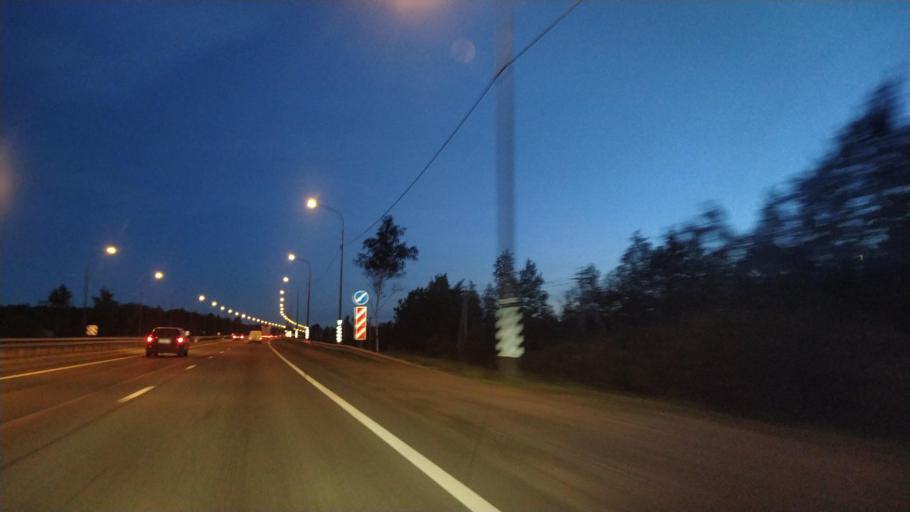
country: RU
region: Leningrad
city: Staraya
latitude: 59.8909
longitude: 30.6393
